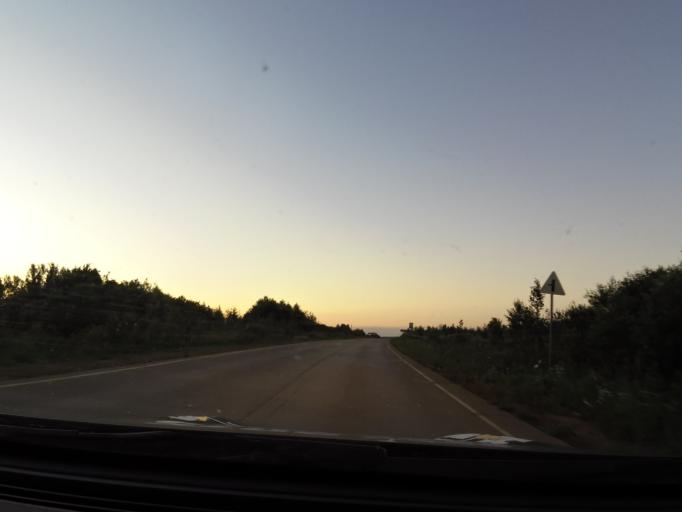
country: RU
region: Vologda
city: Vytegra
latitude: 60.8845
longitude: 36.0389
